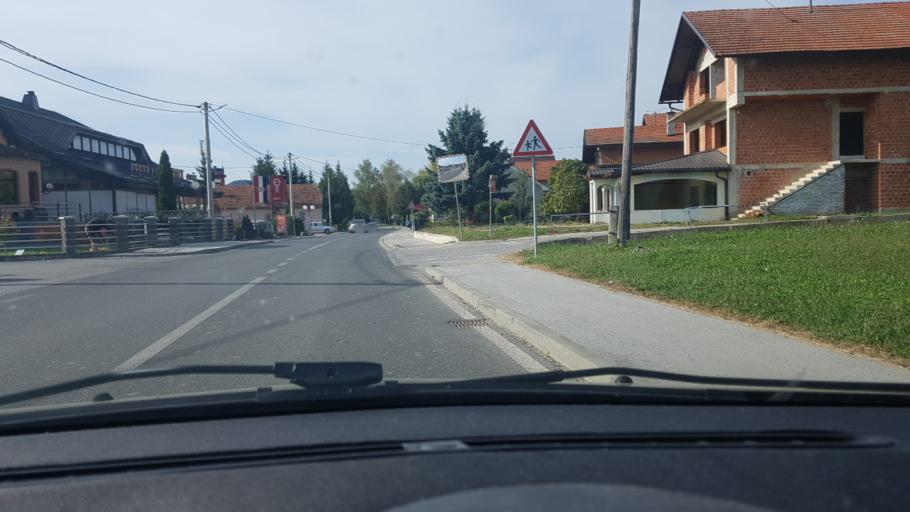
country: HR
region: Krapinsko-Zagorska
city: Zlatar
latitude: 46.0922
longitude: 16.0451
